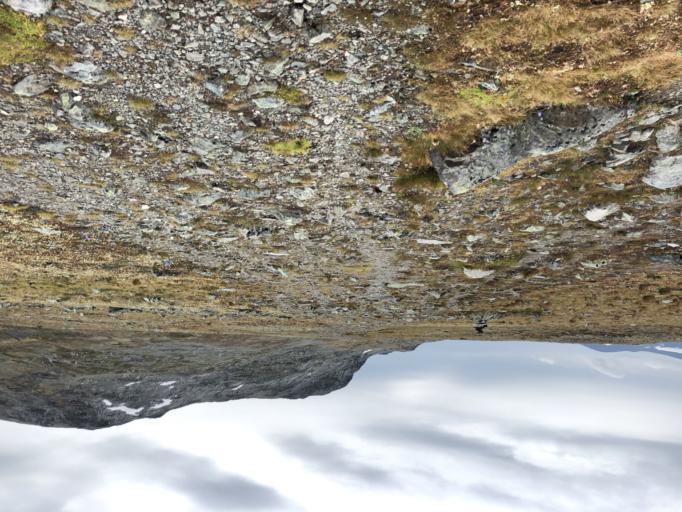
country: NO
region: Oppland
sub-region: Lom
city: Fossbergom
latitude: 61.5242
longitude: 8.8102
